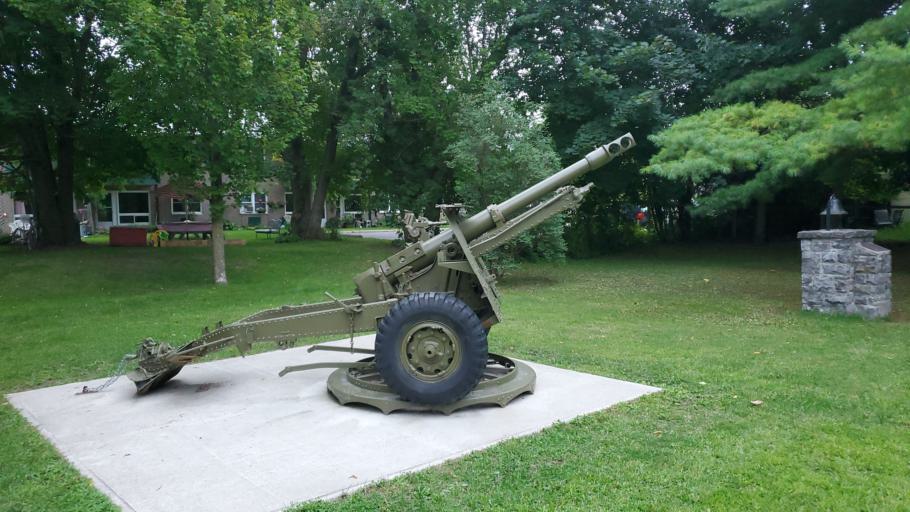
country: CA
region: Ontario
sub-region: Lanark County
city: Smiths Falls
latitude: 44.9138
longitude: -75.8360
